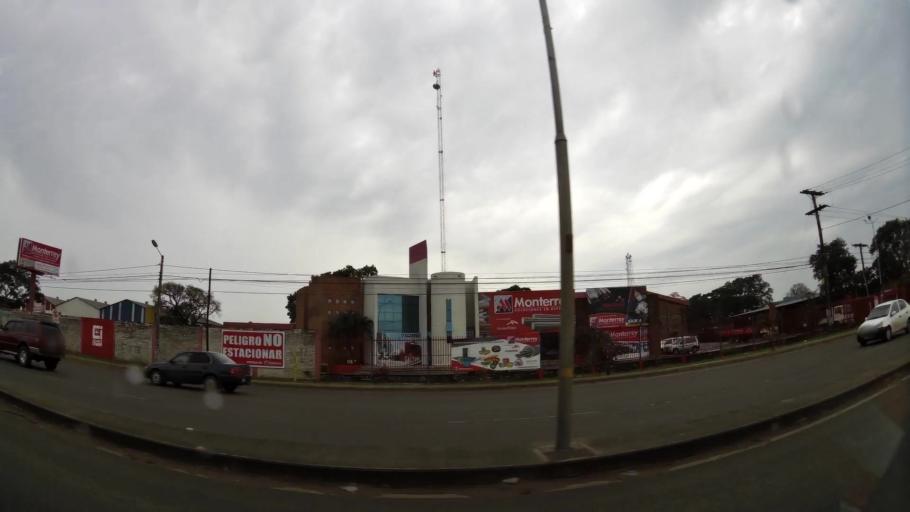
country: BO
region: Santa Cruz
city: Santa Cruz de la Sierra
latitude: -17.7769
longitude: -63.1398
